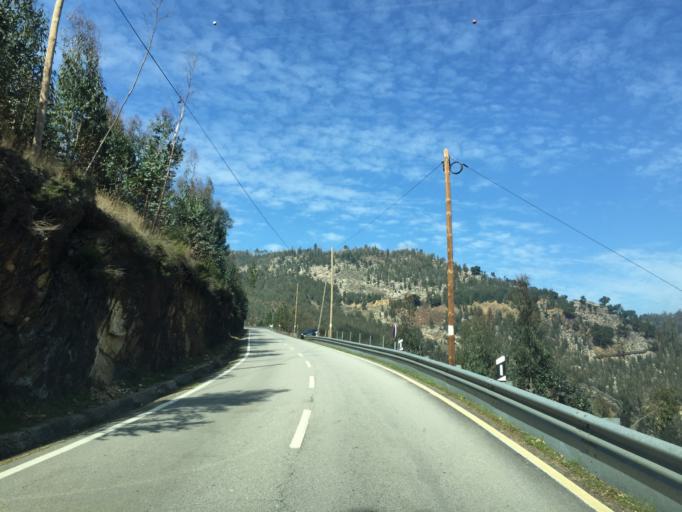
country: PT
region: Aveiro
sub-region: Arouca
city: Arouca
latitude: 40.9546
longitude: -8.1744
